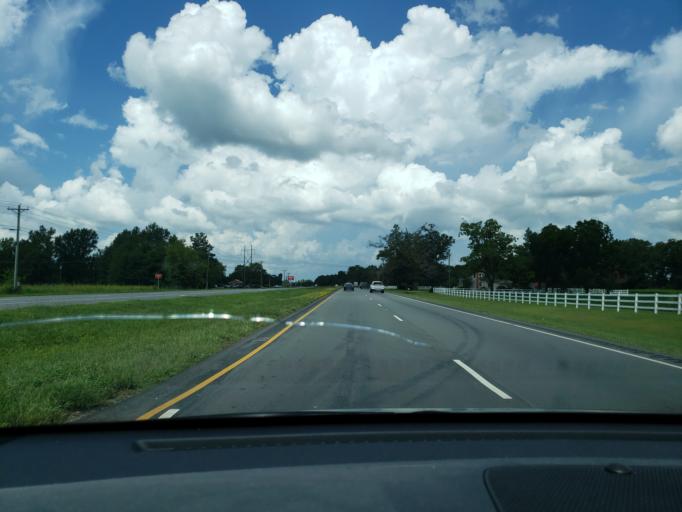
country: US
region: North Carolina
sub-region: Robeson County
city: Saint Pauls
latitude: 34.7717
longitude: -78.8103
